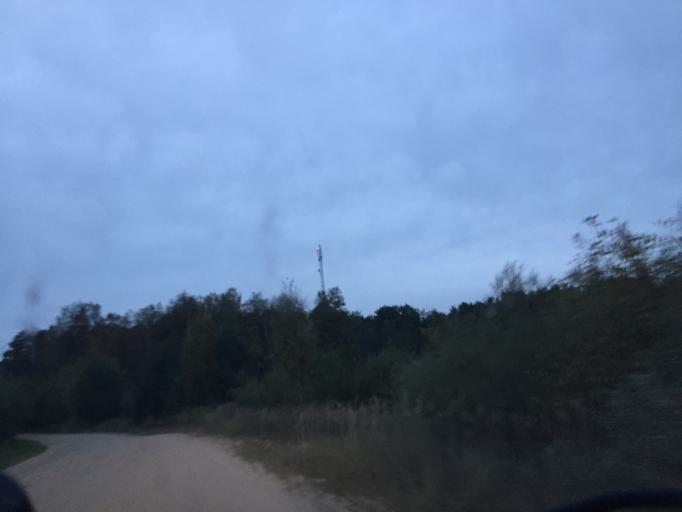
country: LV
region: Adazi
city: Adazi
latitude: 57.0887
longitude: 24.3719
